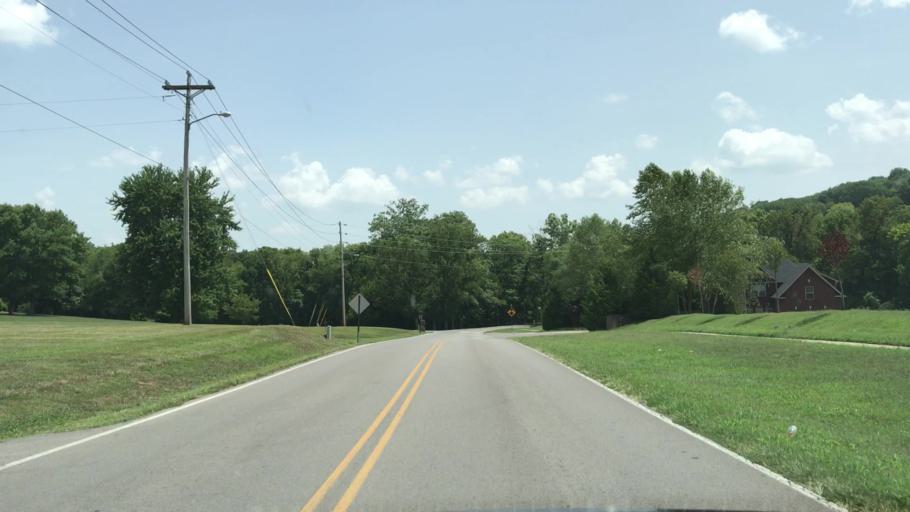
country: US
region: Tennessee
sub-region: Rutherford County
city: La Vergne
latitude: 35.9569
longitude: -86.5989
